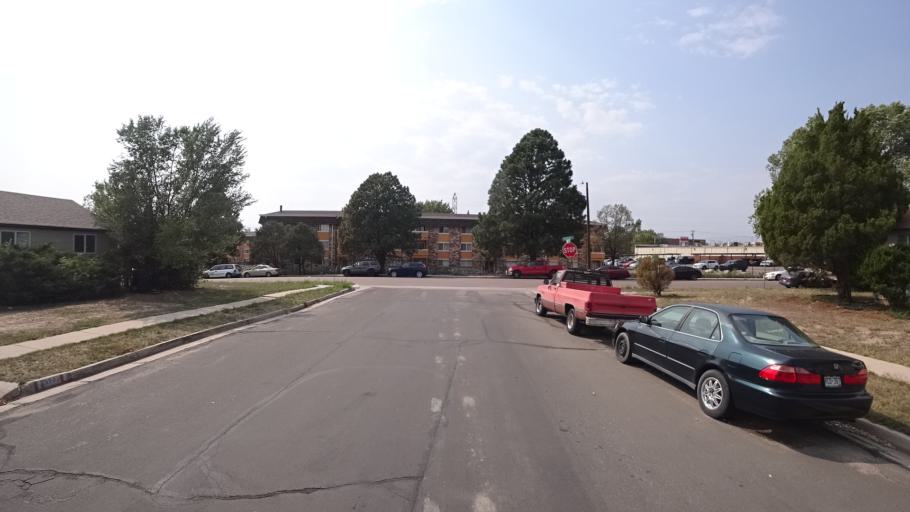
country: US
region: Colorado
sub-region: El Paso County
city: Stratmoor
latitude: 38.8303
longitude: -104.7556
